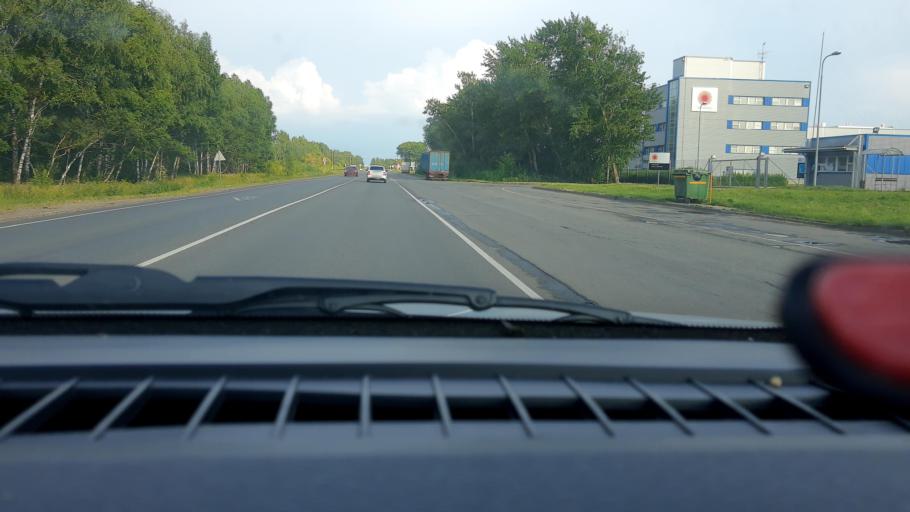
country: RU
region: Nizjnij Novgorod
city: Arzamas
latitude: 55.3012
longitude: 43.9262
